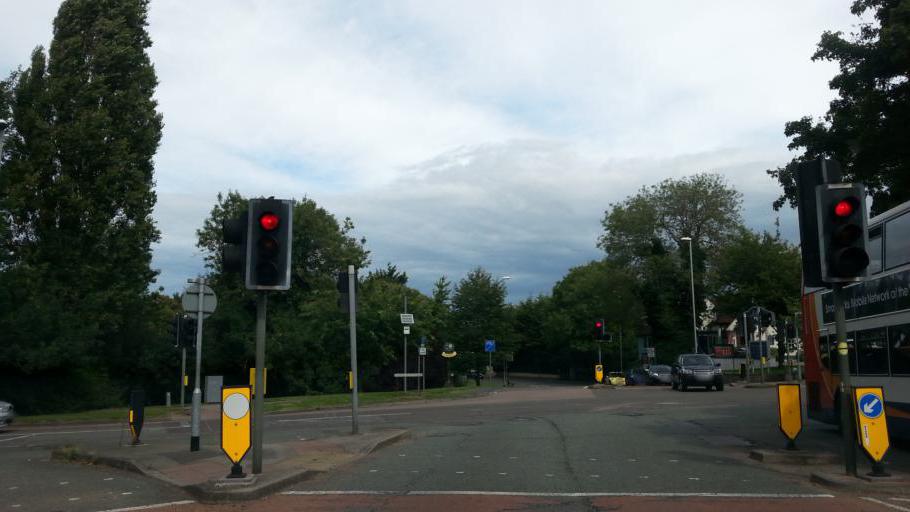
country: GB
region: England
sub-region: Cambridgeshire
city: Fulbourn
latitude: 52.1837
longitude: 0.1711
